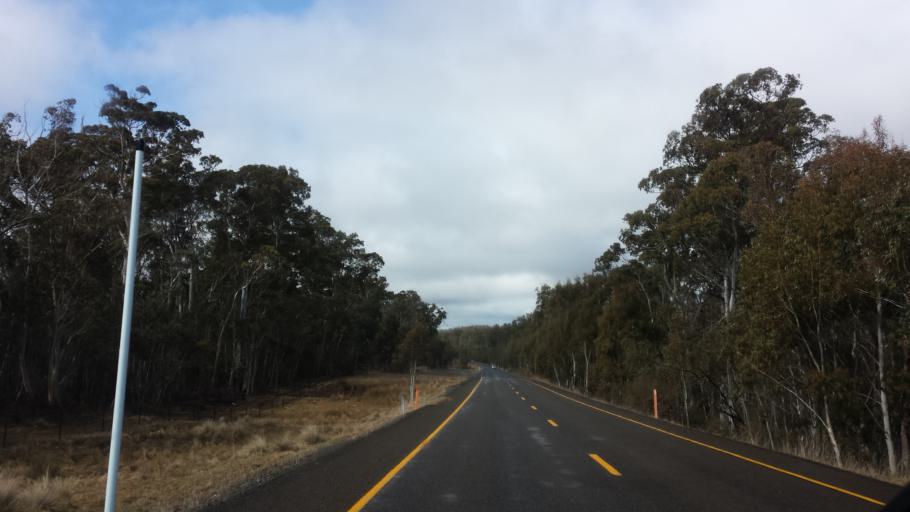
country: AU
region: Victoria
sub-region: Alpine
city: Mount Beauty
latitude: -37.0649
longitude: 147.3388
